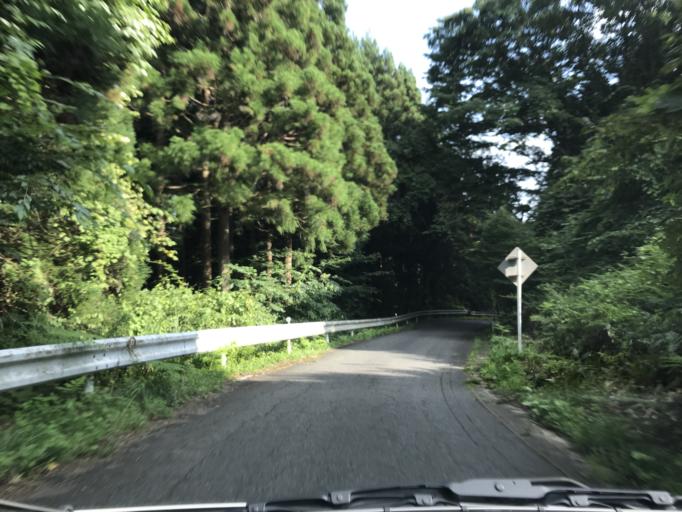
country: JP
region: Iwate
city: Ofunato
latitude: 38.9801
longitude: 141.4679
